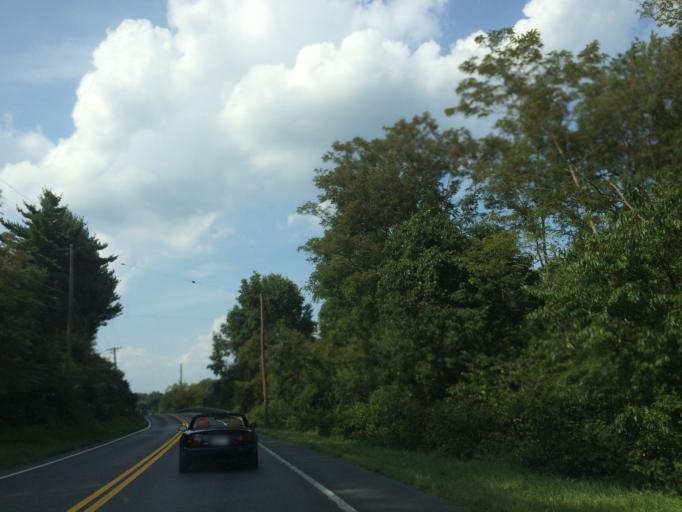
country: US
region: Maryland
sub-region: Carroll County
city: Sykesville
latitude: 39.4118
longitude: -77.0121
